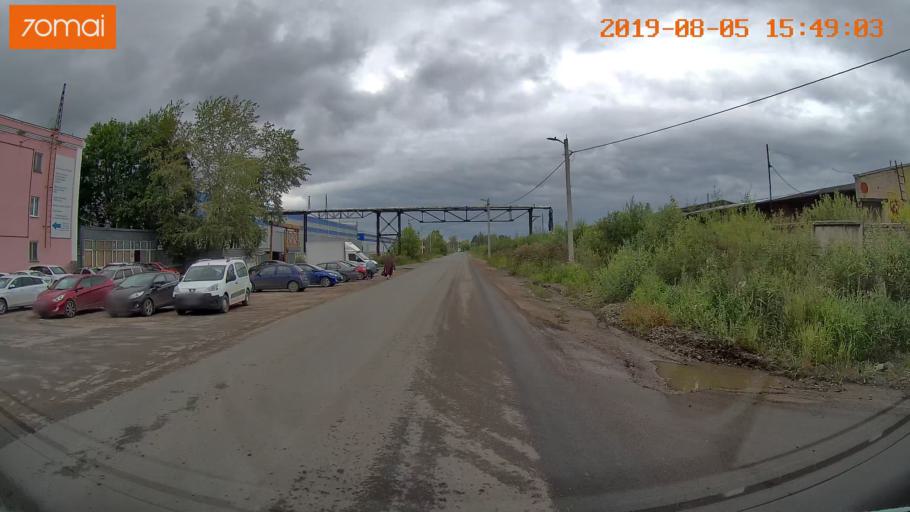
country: RU
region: Ivanovo
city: Novo-Talitsy
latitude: 56.9911
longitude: 40.9089
